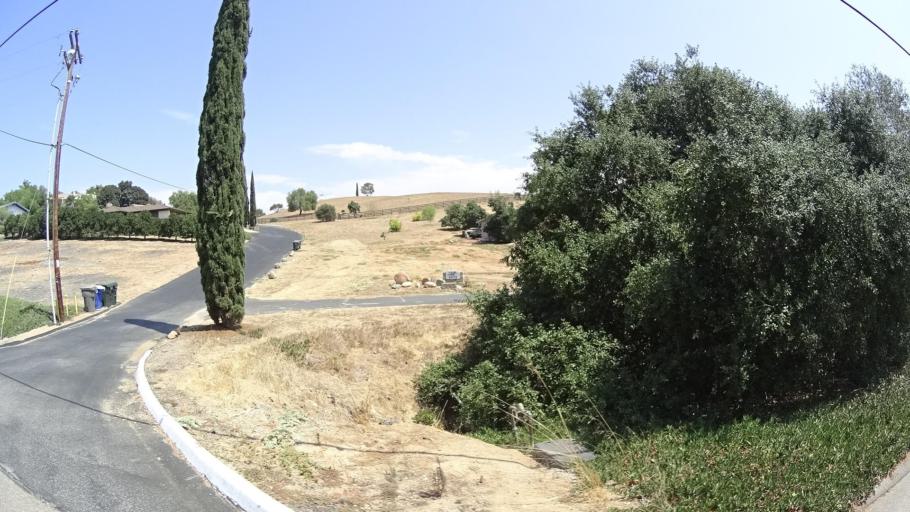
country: US
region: California
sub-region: San Diego County
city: Bonsall
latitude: 33.3188
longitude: -117.2085
